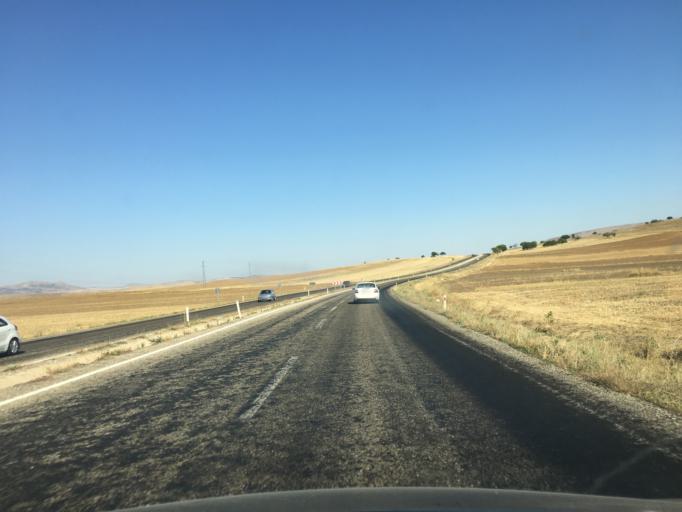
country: TR
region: Kirsehir
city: Akpinar
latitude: 39.3600
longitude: 33.9177
